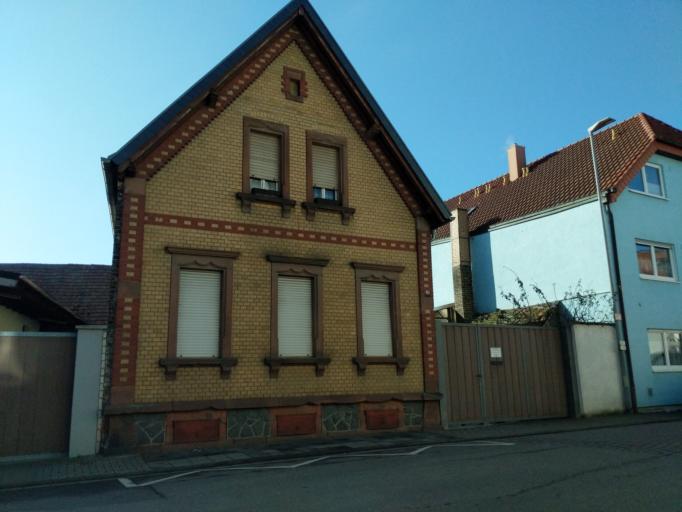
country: DE
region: Rheinland-Pfalz
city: Frankenthal
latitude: 49.5513
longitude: 8.3782
